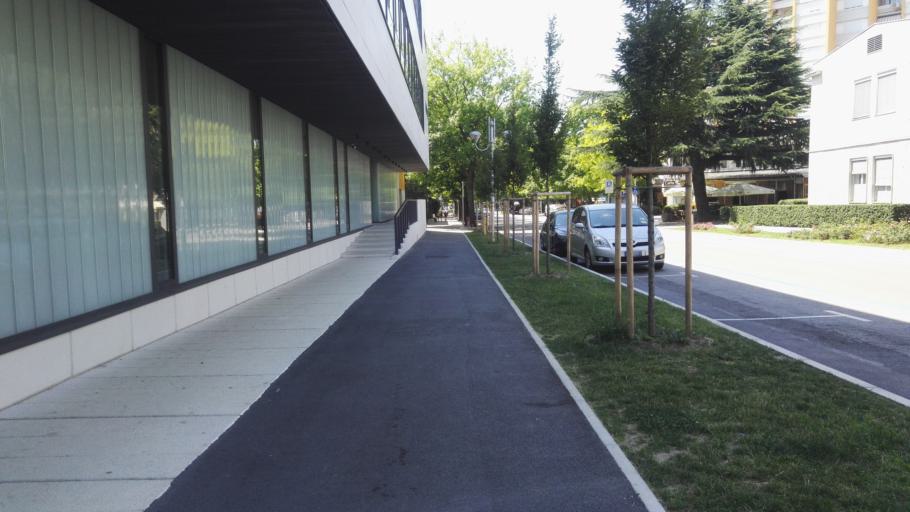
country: SI
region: Nova Gorica
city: Nova Gorica
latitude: 45.9576
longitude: 13.6455
